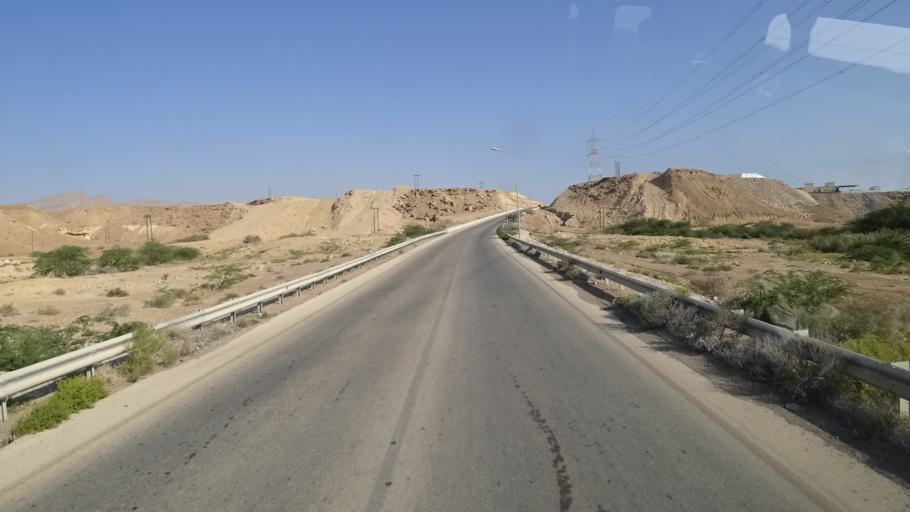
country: OM
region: Ash Sharqiyah
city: Sur
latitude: 22.5835
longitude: 59.4574
